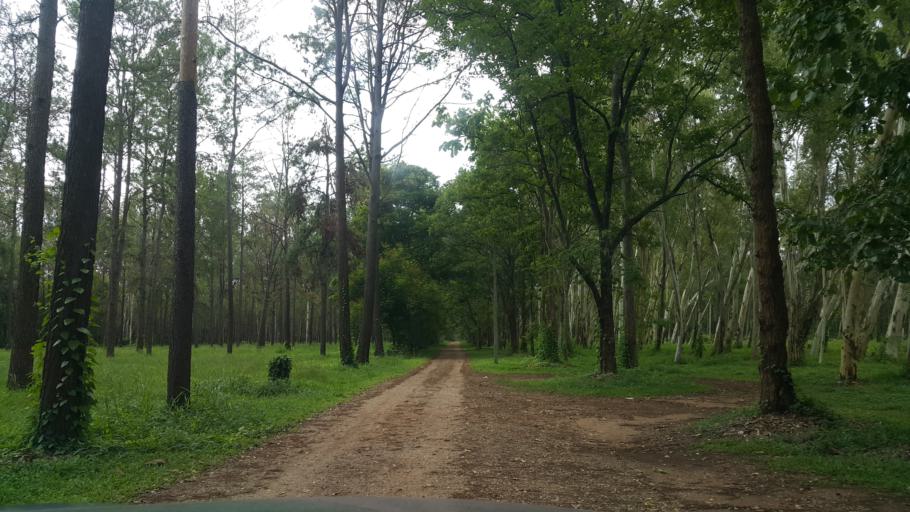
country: TH
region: Chiang Mai
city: Mae Taeng
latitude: 19.1529
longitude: 98.9484
